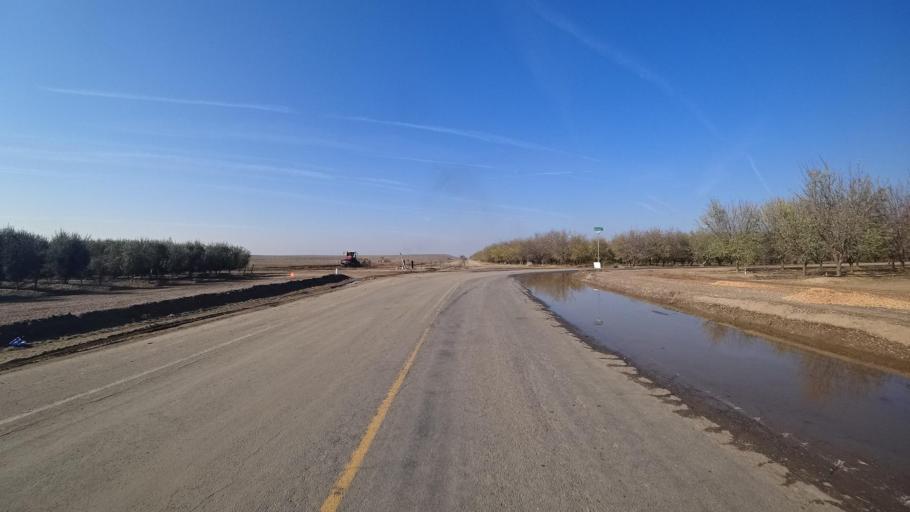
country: US
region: California
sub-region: Kern County
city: Weedpatch
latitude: 35.1942
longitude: -118.8957
